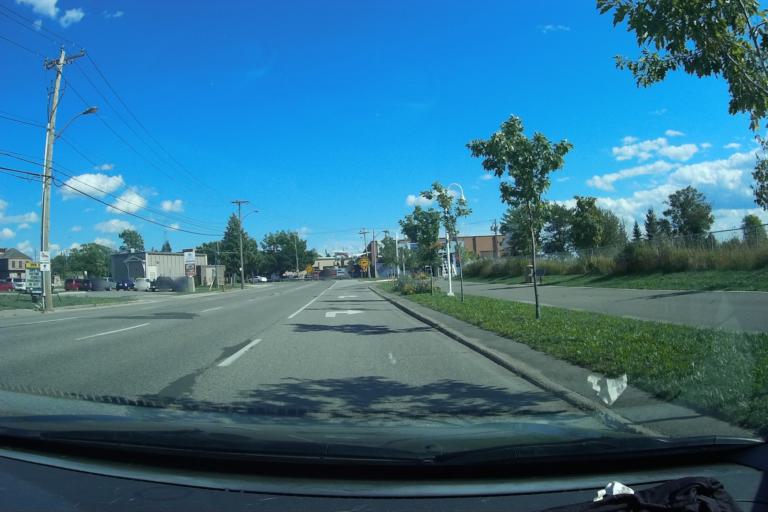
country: CA
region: Ontario
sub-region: Algoma
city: Sault Ste. Marie
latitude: 46.5058
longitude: -84.3262
